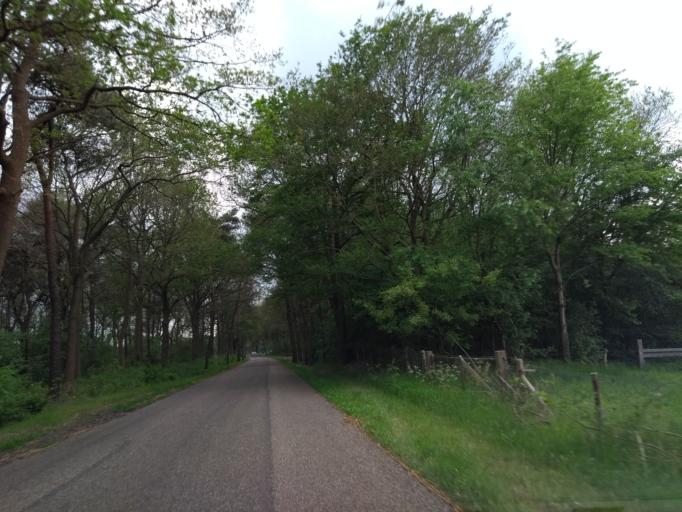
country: NL
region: Overijssel
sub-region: Gemeente Staphorst
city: Staphorst
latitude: 52.6410
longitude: 6.2831
